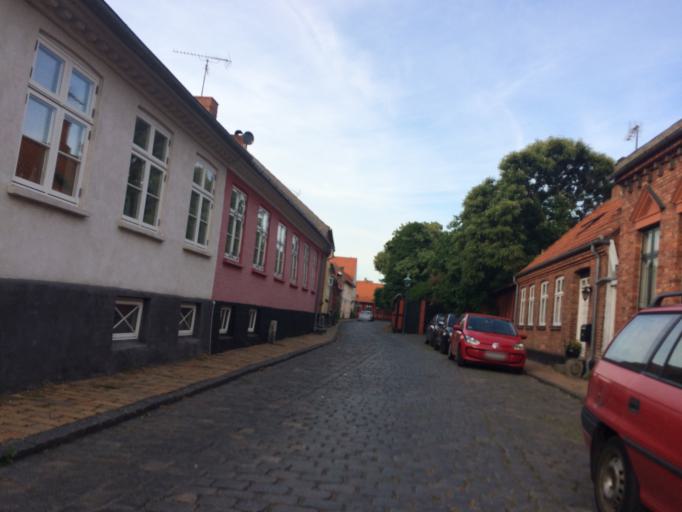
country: DK
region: Capital Region
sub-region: Bornholm Kommune
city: Ronne
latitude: 55.0990
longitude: 14.6999
